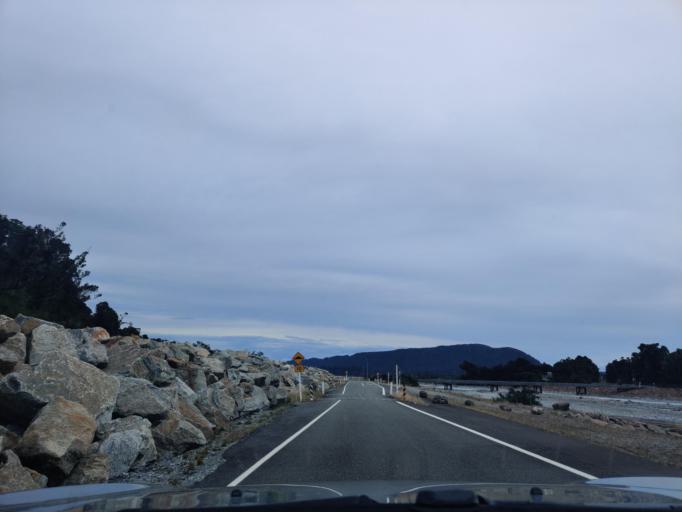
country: NZ
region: West Coast
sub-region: Westland District
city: Hokitika
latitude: -43.3961
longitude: 170.1811
